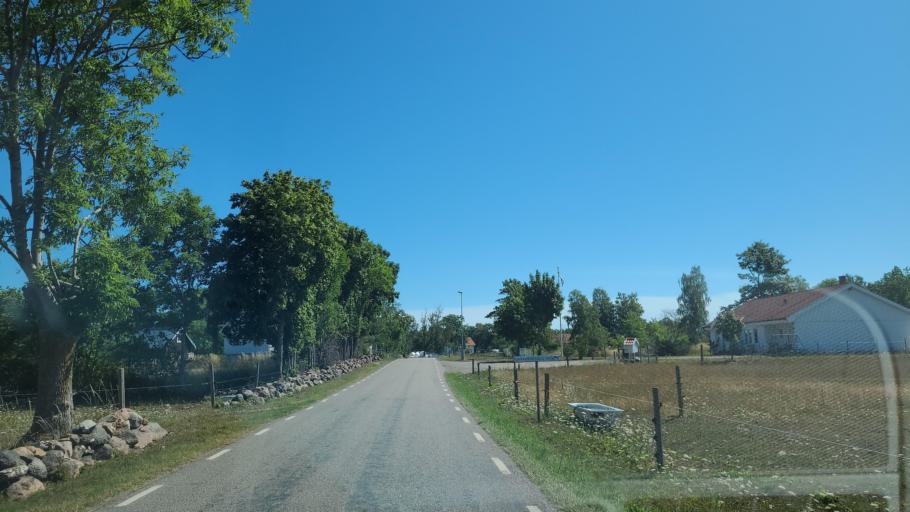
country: SE
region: Kalmar
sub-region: Borgholms Kommun
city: Borgholm
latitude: 56.7454
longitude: 16.6962
